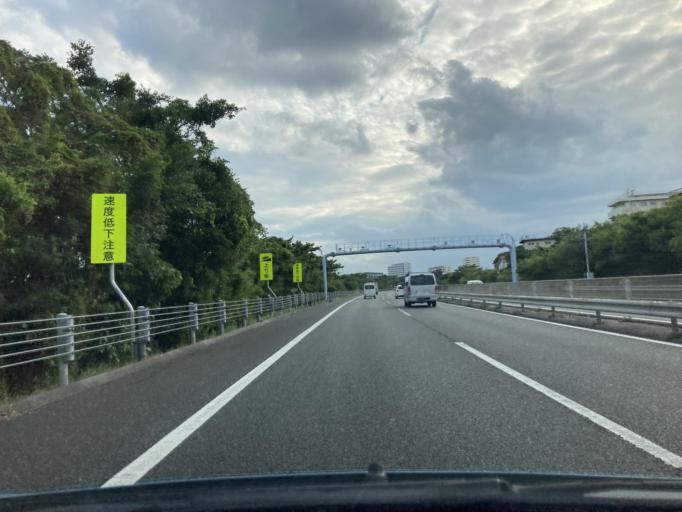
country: JP
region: Okinawa
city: Ginowan
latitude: 26.2634
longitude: 127.7730
